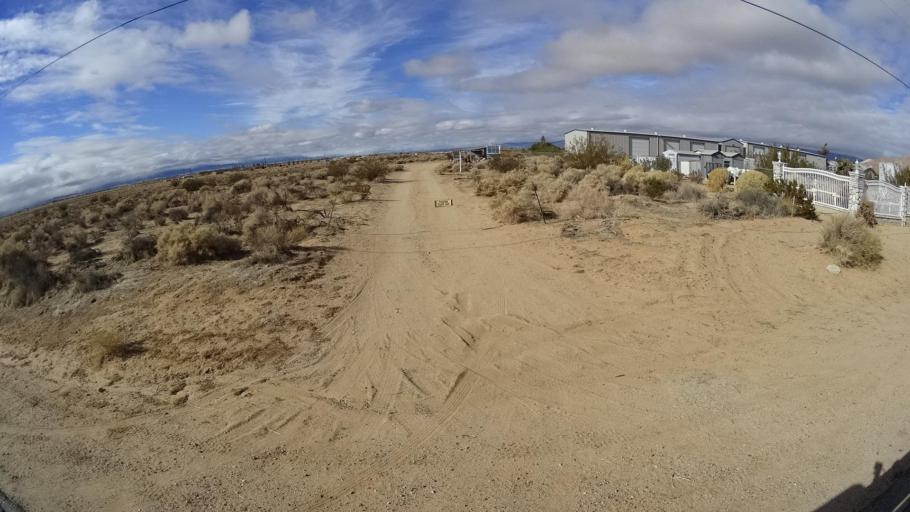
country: US
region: California
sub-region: Kern County
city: Rosamond
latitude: 34.8607
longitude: -118.2734
